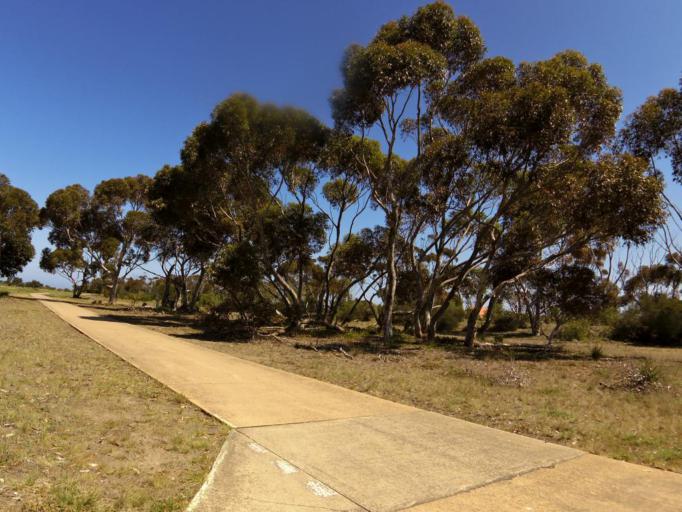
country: AU
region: Victoria
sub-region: Hobsons Bay
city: Altona Meadows
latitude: -37.8828
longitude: 144.7947
